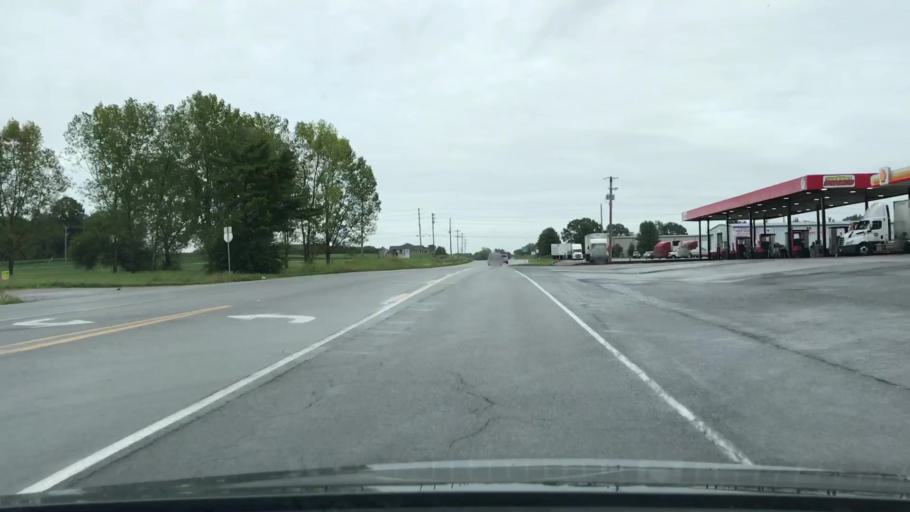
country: US
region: Kentucky
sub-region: Simpson County
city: Franklin
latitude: 36.7156
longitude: -86.5198
